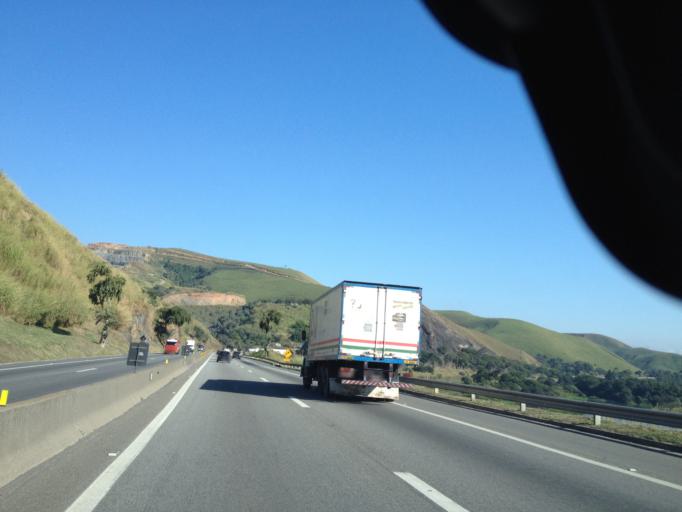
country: BR
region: Rio de Janeiro
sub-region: Porto Real
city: Porto Real
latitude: -22.4867
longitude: -44.2491
